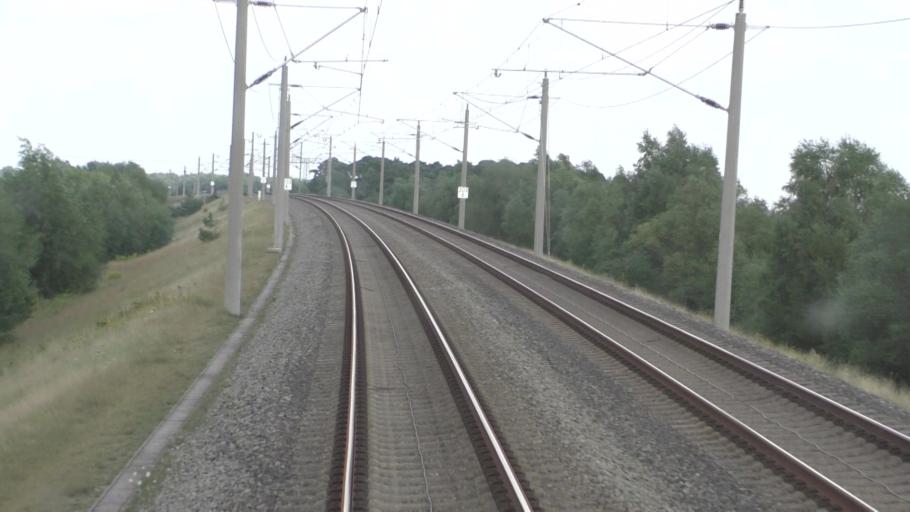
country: DE
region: Saxony-Anhalt
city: Stendal
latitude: 52.5794
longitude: 11.8981
